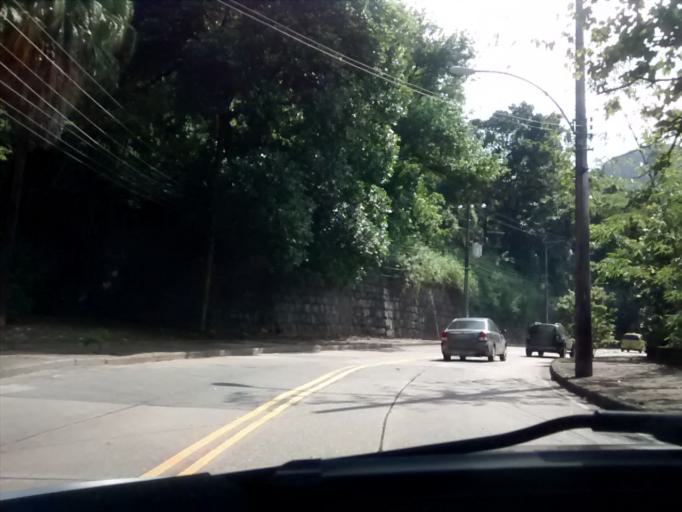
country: BR
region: Rio de Janeiro
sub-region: Rio De Janeiro
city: Rio de Janeiro
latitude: -22.9508
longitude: -43.2583
